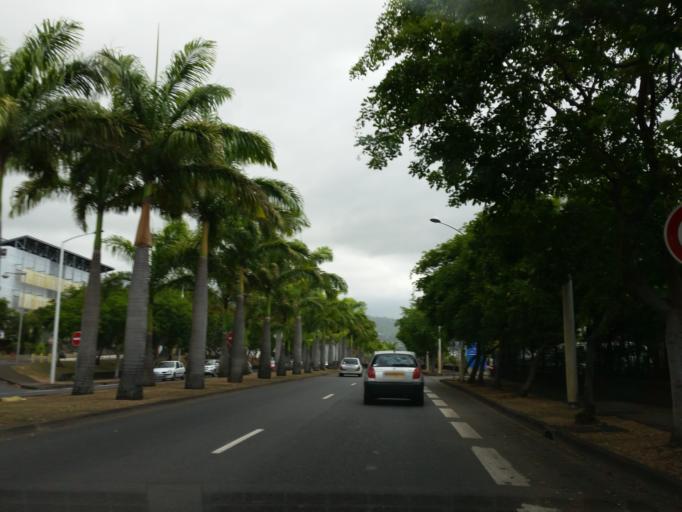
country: RE
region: Reunion
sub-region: Reunion
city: Sainte-Marie
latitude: -20.9023
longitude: 55.5025
